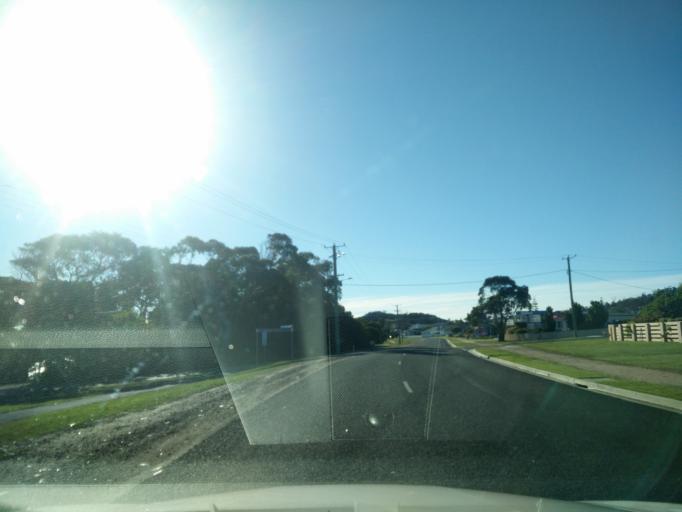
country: AU
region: Tasmania
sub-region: Break O'Day
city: St Helens
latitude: -41.8704
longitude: 148.2940
